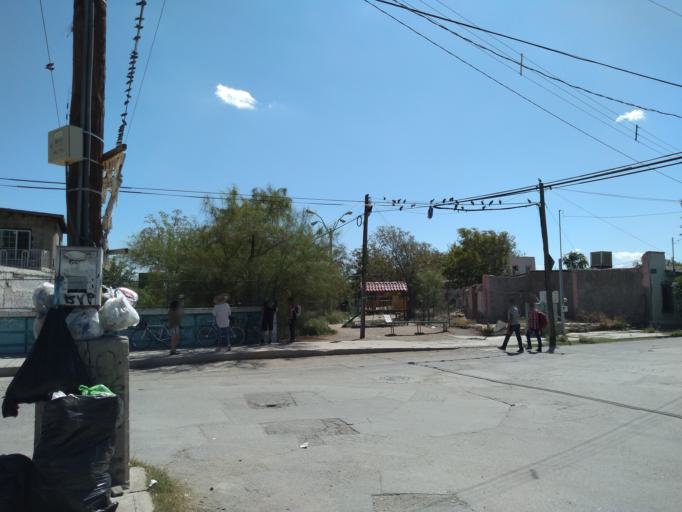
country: US
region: Texas
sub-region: El Paso County
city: El Paso
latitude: 31.7468
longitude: -106.4927
